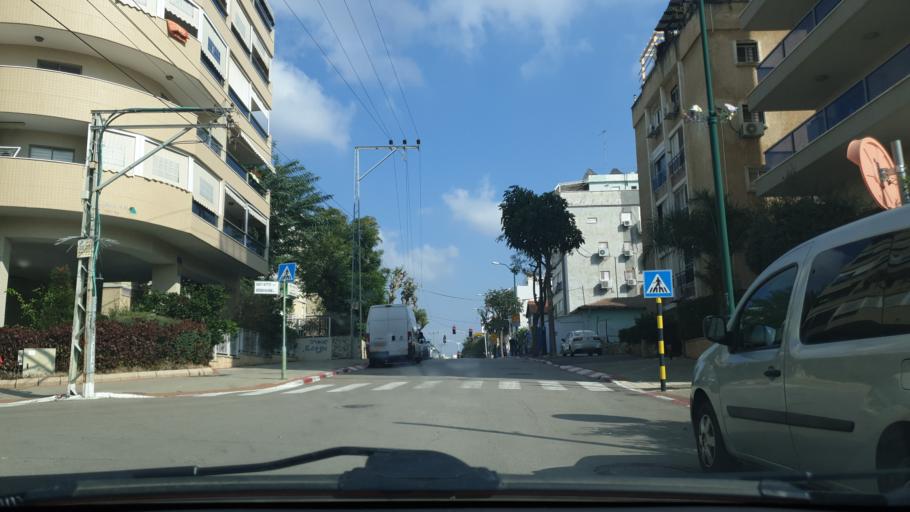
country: IL
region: Central District
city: Rishon LeZiyyon
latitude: 31.9672
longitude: 34.8123
